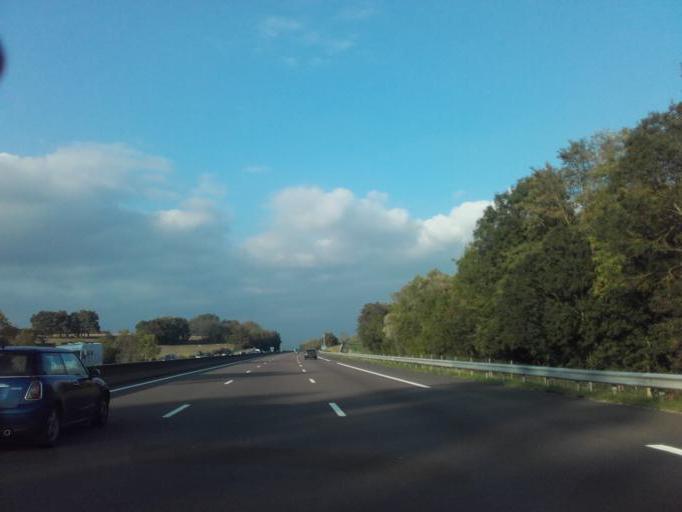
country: FR
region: Bourgogne
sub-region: Departement de Saone-et-Loire
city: Tournus
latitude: 46.5199
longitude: 4.9147
